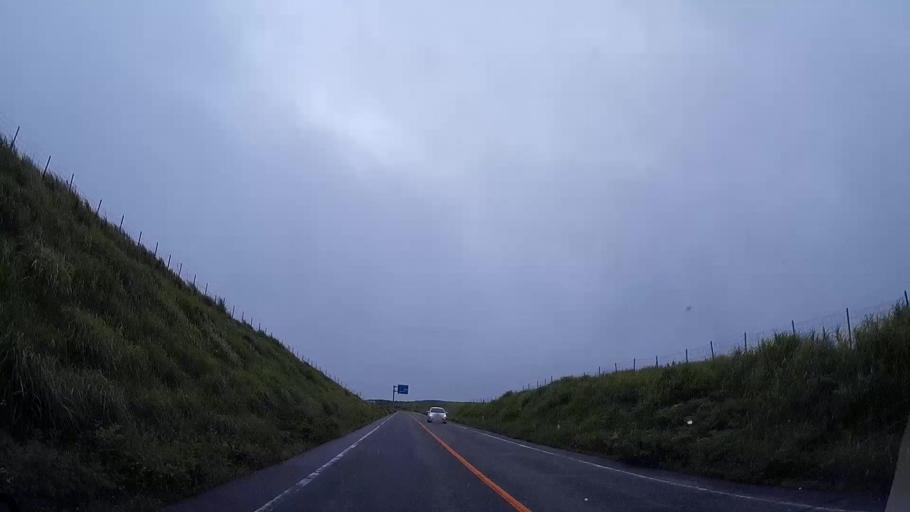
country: JP
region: Kumamoto
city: Aso
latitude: 33.0037
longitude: 131.0705
